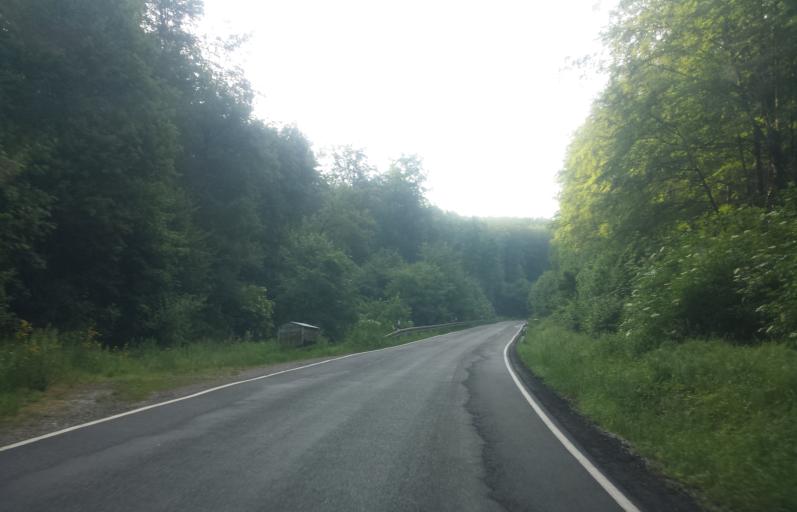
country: DE
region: Bavaria
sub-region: Upper Franconia
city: Ebermannstadt
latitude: 49.7829
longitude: 11.2203
